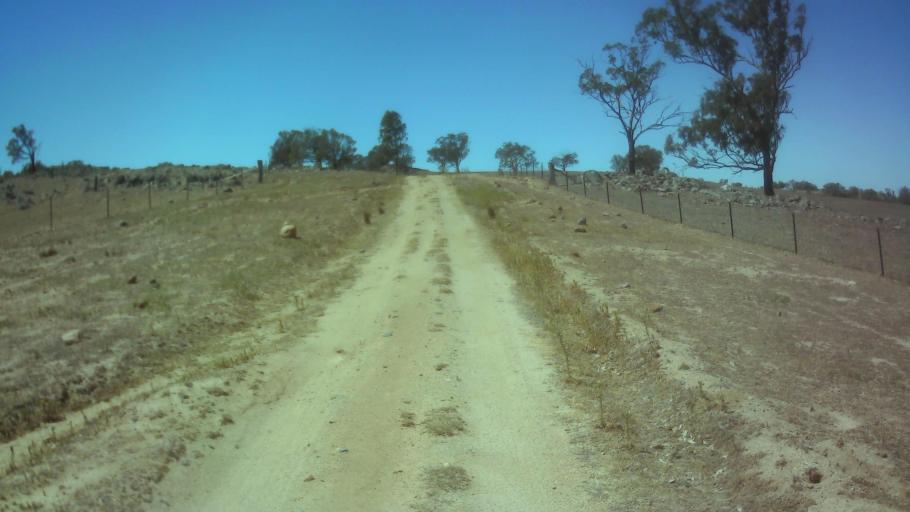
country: AU
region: New South Wales
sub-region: Cowra
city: Cowra
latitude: -33.8939
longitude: 148.5014
